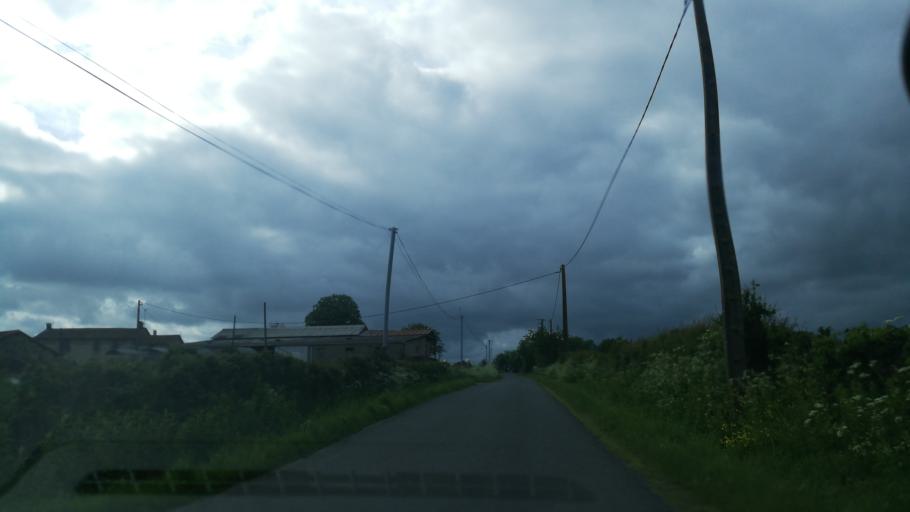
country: FR
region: Poitou-Charentes
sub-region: Departement des Deux-Sevres
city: Moncoutant
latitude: 46.7091
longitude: -0.5859
